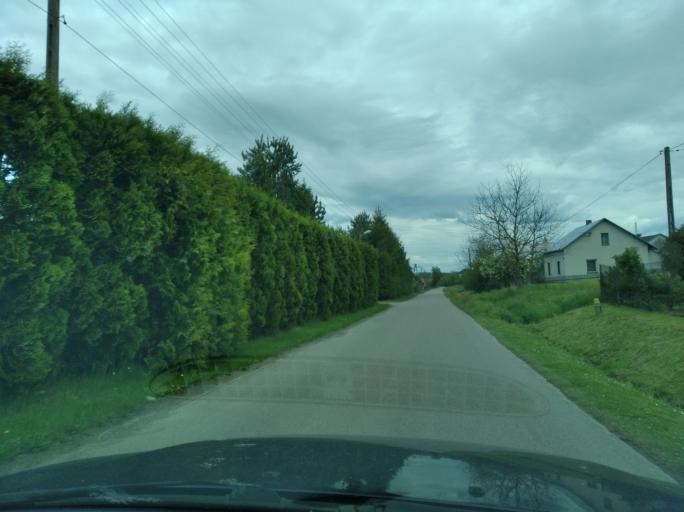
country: PL
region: Subcarpathian Voivodeship
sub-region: Powiat przeworski
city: Jawornik Polski
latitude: 49.8362
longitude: 22.3007
